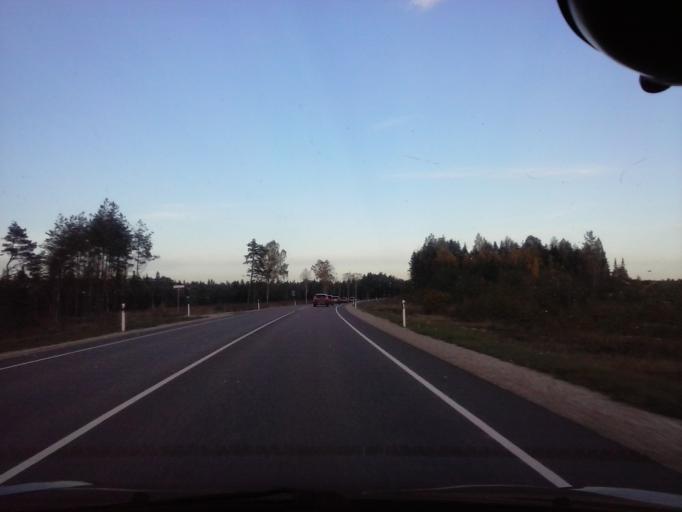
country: EE
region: Harju
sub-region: Nissi vald
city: Turba
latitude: 58.9780
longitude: 23.9576
